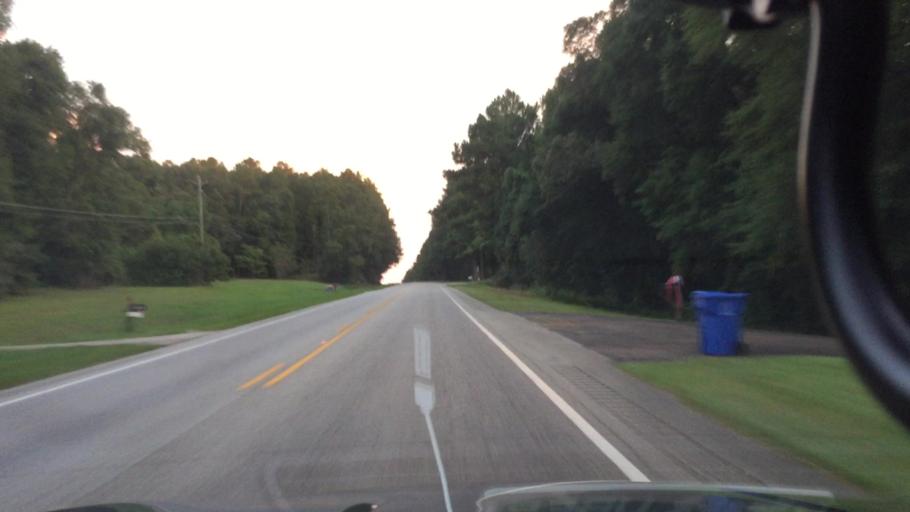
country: US
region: Alabama
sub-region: Coffee County
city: New Brockton
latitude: 31.3984
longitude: -85.8799
